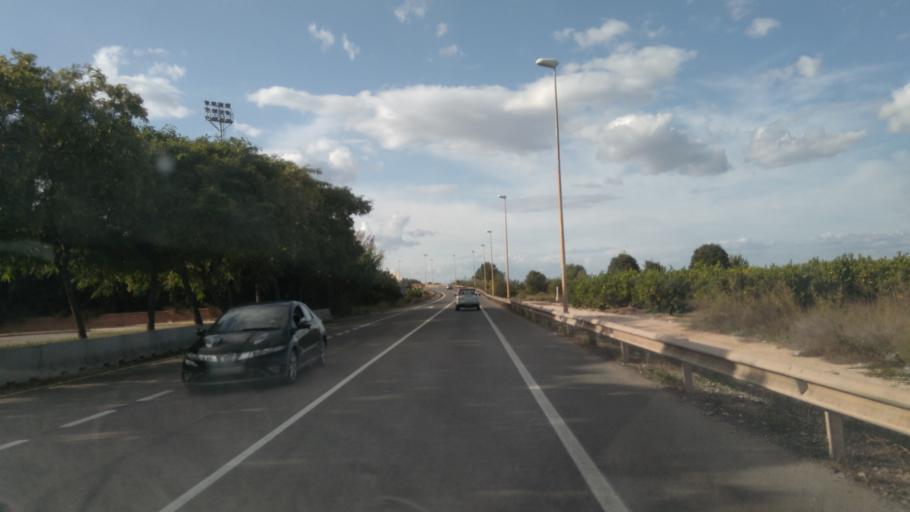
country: ES
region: Valencia
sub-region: Provincia de Valencia
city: Alzira
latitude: 39.1610
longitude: -0.4327
